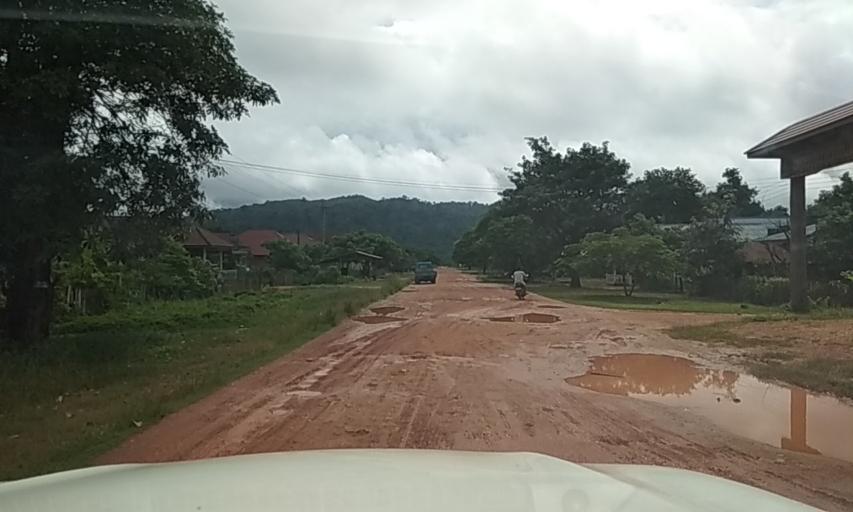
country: LA
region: Bolikhamxai
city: Bolikhan
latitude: 18.5571
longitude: 103.7340
